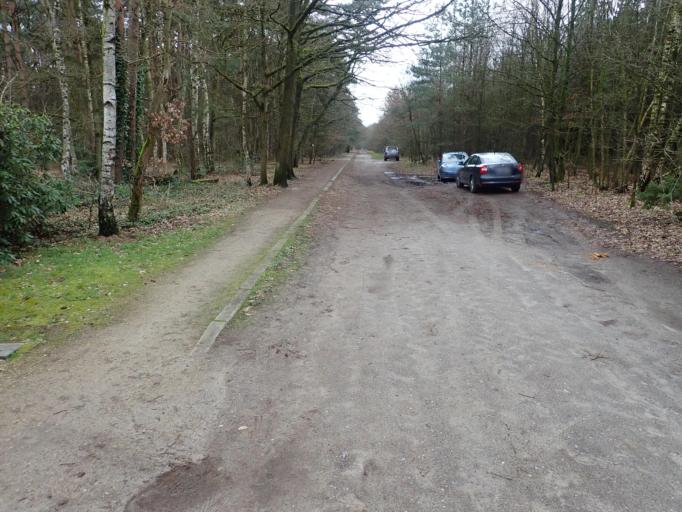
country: BE
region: Flanders
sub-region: Provincie Antwerpen
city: Schilde
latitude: 51.2873
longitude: 4.6033
